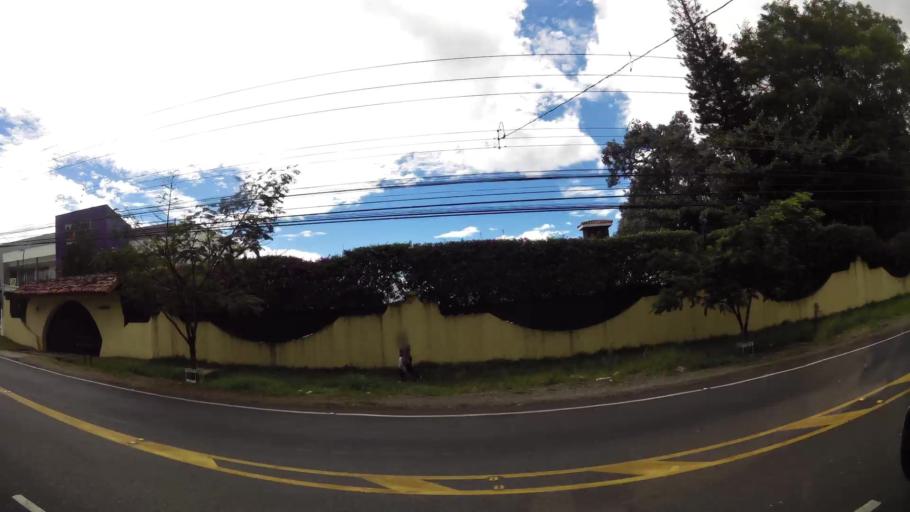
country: CR
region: Cartago
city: San Diego
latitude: 9.9108
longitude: -84.0135
